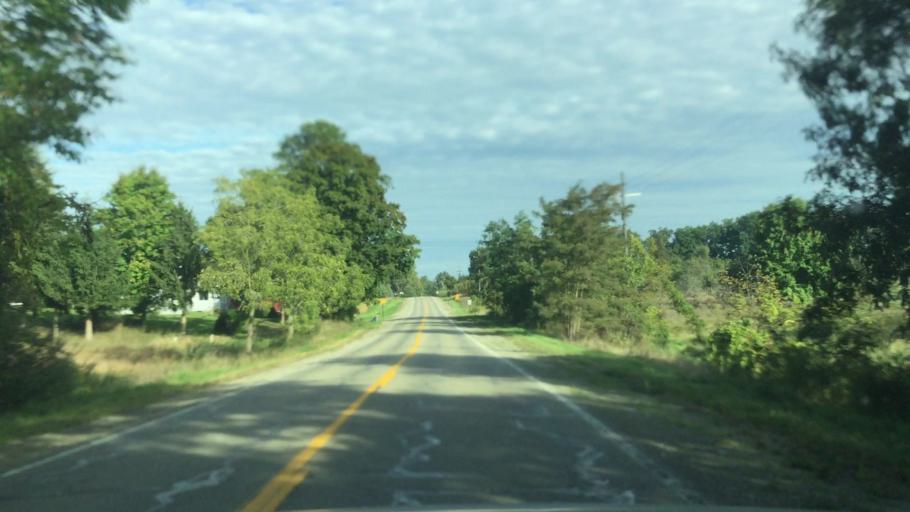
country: US
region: Michigan
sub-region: Livingston County
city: Howell
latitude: 42.5523
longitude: -83.8829
